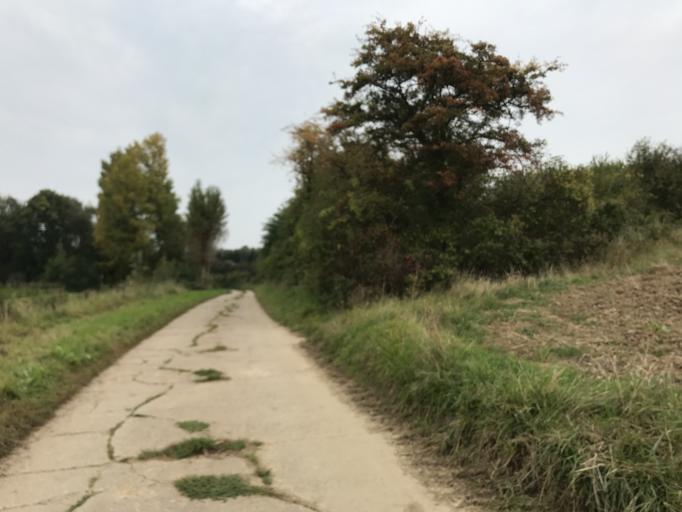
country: DE
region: Rheinland-Pfalz
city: Klein-Winternheim
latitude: 49.9319
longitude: 8.2203
